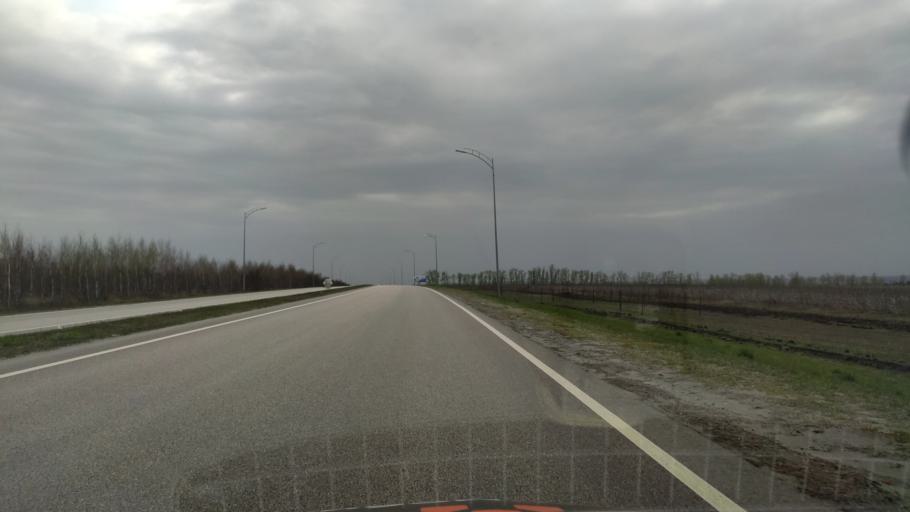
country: RU
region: Belgorod
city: Staryy Oskol
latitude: 51.3806
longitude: 37.8541
